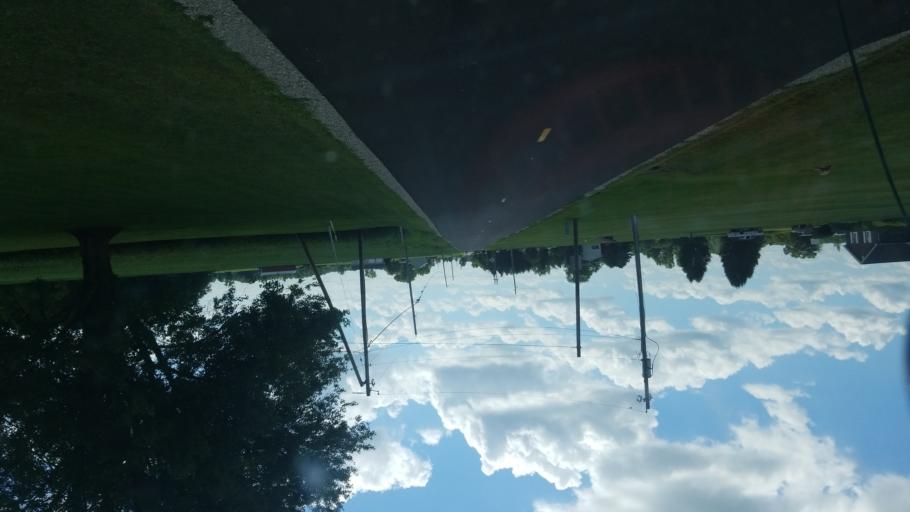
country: US
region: Ohio
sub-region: Marion County
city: Prospect
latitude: 40.5158
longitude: -83.1657
